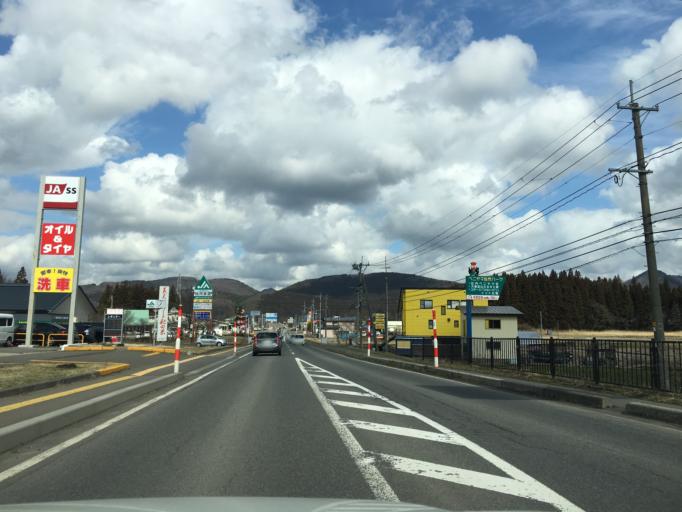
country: JP
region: Akita
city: Odate
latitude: 40.2173
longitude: 140.5847
